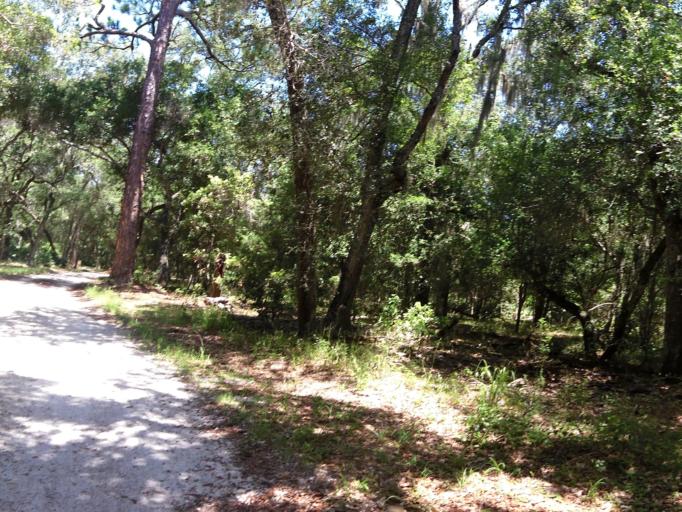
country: US
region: Florida
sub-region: Saint Johns County
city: Villano Beach
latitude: 30.0237
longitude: -81.3352
